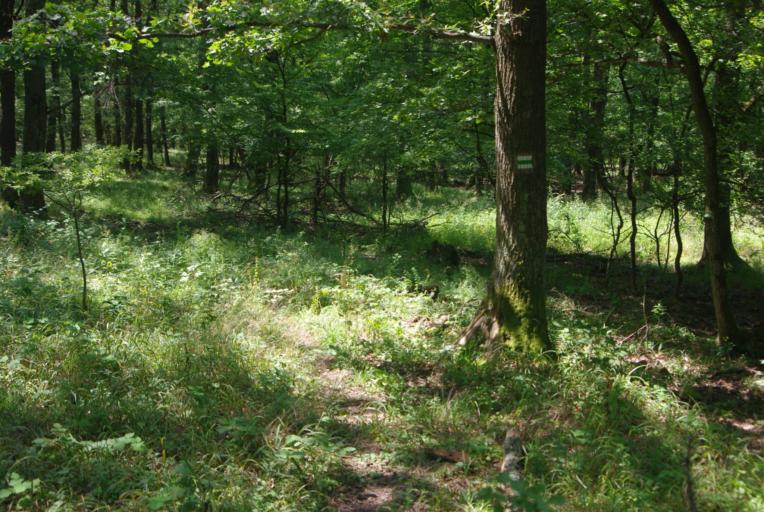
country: HU
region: Borsod-Abauj-Zemplen
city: Gonc
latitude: 48.4073
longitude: 21.3081
